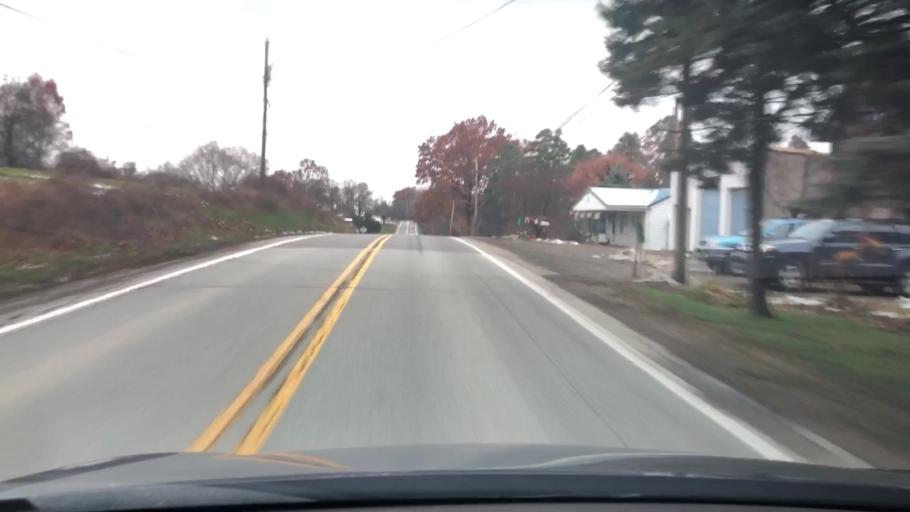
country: US
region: Pennsylvania
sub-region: Armstrong County
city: Kittanning
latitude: 40.8897
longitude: -79.3838
